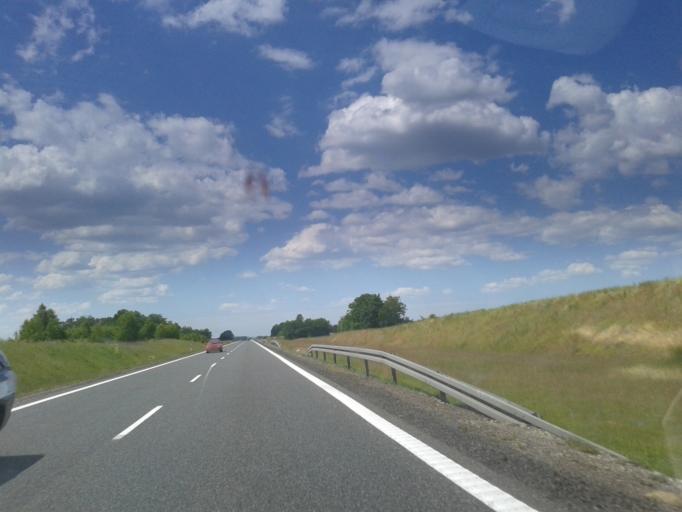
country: PL
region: Pomeranian Voivodeship
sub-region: Powiat chojnicki
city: Chojnice
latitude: 53.6837
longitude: 17.5182
